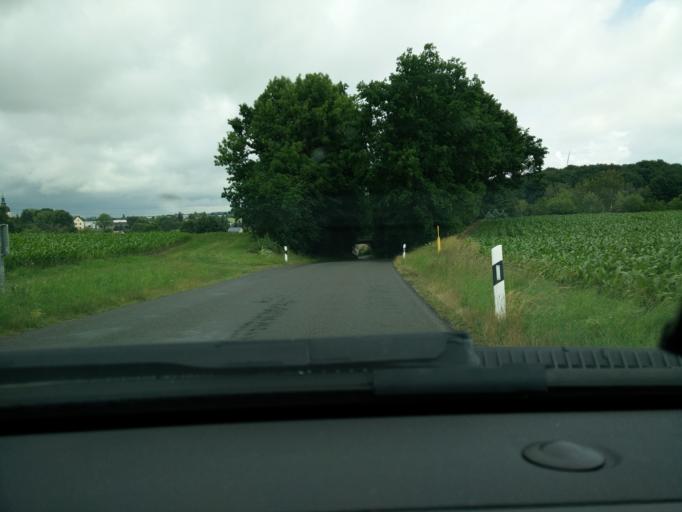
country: DE
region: Saxony
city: Geithain
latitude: 51.0837
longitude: 12.6899
